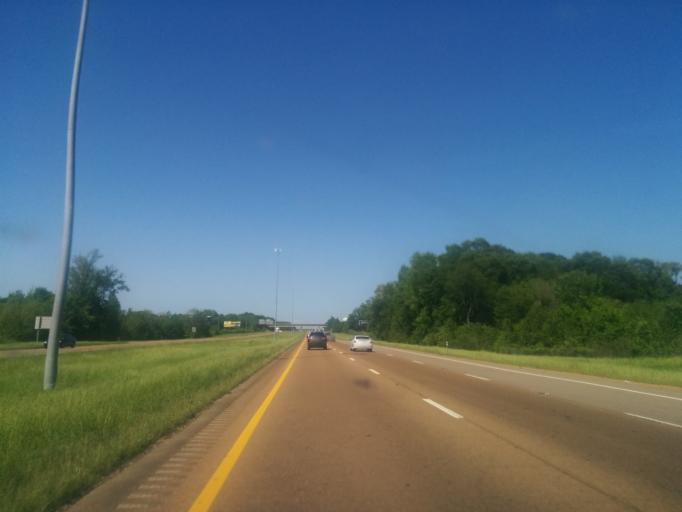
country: US
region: Mississippi
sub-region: Madison County
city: Madison
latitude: 32.5451
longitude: -90.0924
